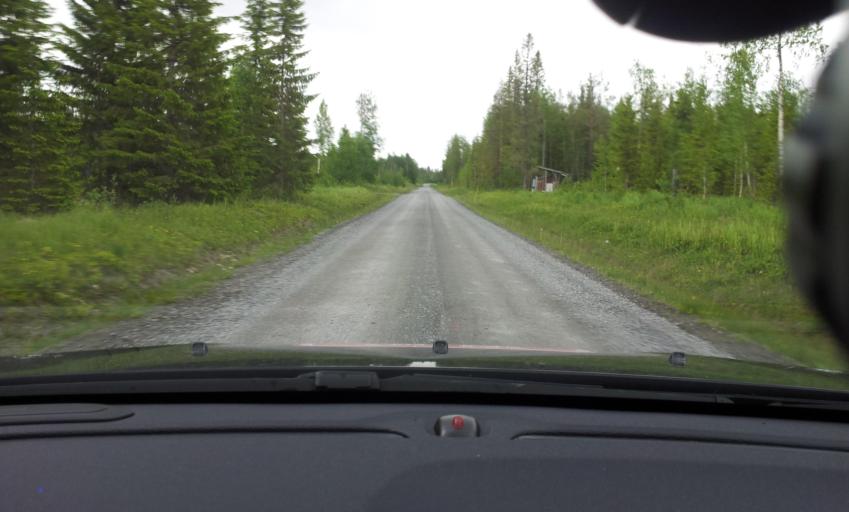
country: SE
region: Jaemtland
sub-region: OEstersunds Kommun
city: Brunflo
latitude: 63.1432
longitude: 15.0520
